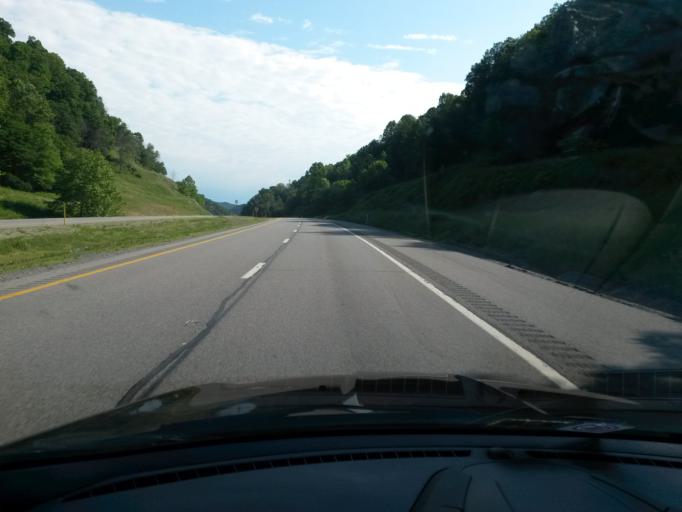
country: US
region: West Virginia
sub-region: Braxton County
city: Sutton
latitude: 38.7738
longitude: -80.6737
